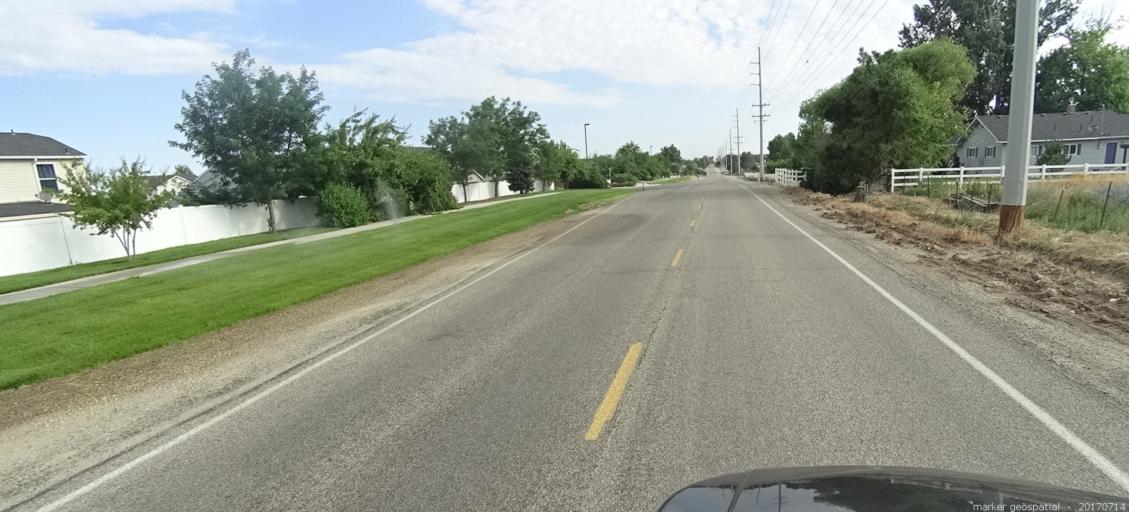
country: US
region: Idaho
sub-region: Ada County
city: Kuna
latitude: 43.4777
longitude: -116.4137
